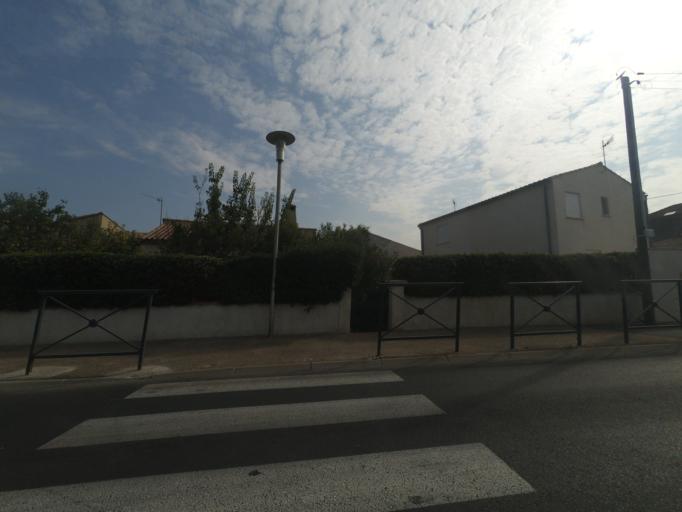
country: FR
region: Languedoc-Roussillon
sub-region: Departement de l'Herault
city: Lunel
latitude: 43.6825
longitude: 4.1336
